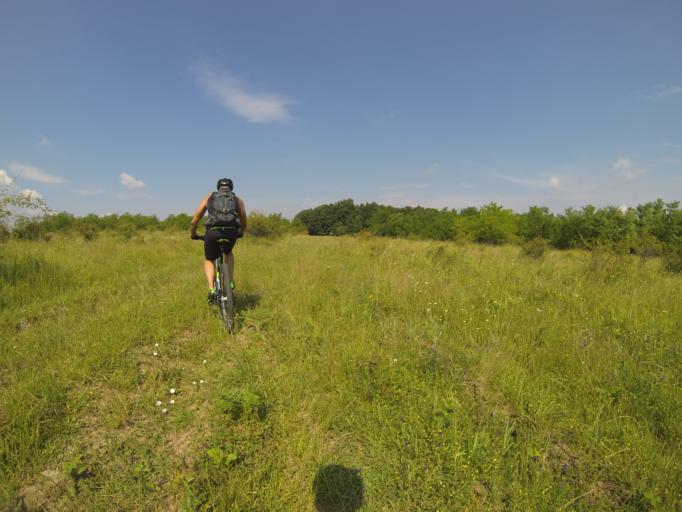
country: RO
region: Gorj
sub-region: Comuna Crusetu
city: Crusetu
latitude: 44.6108
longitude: 23.6509
